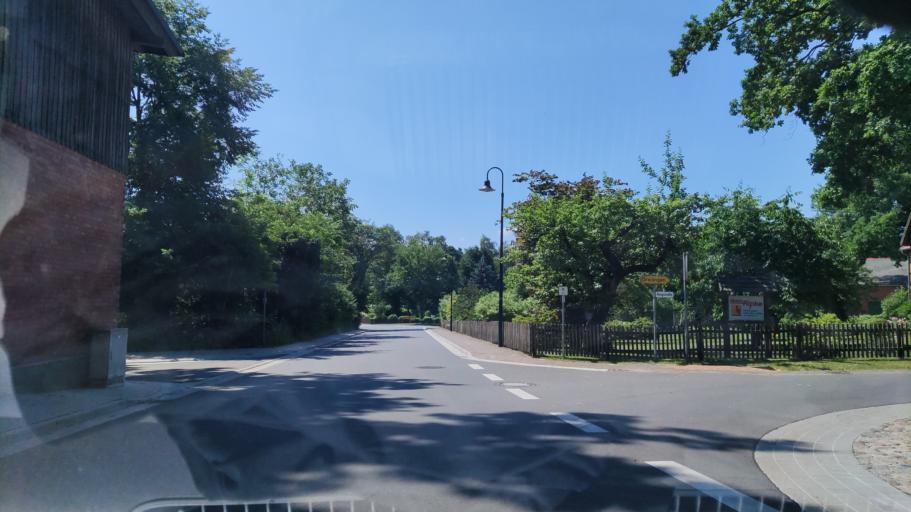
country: DE
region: Lower Saxony
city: Suderburg
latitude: 52.8761
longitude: 10.4072
